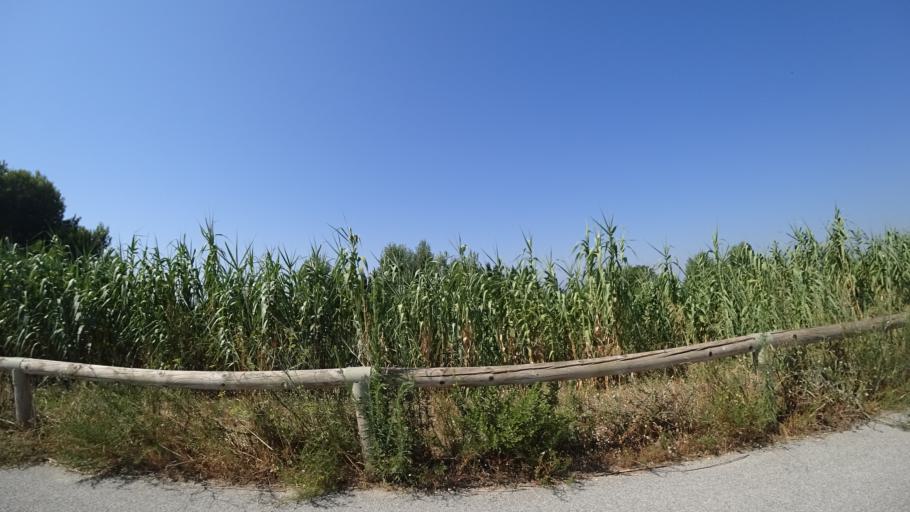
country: FR
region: Languedoc-Roussillon
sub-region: Departement des Pyrenees-Orientales
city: Claira
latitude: 42.7553
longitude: 2.9392
